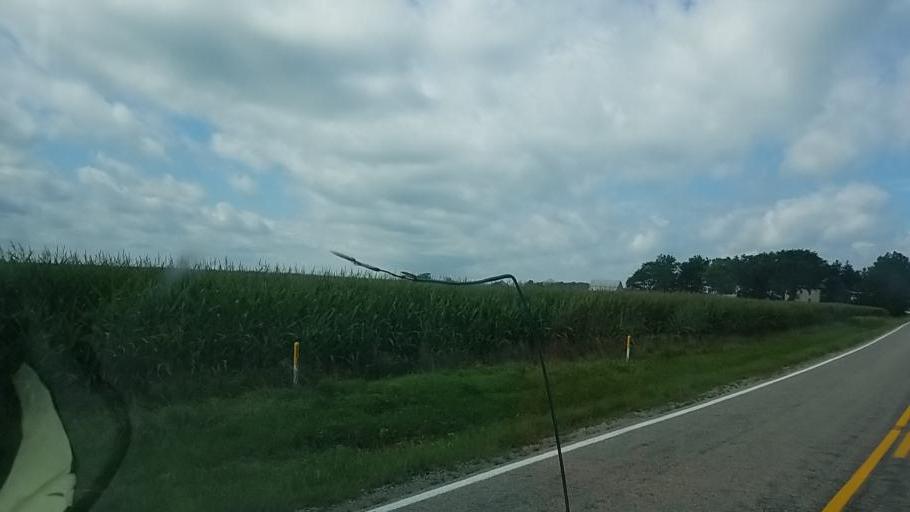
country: US
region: Ohio
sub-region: Madison County
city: Bethel
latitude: 39.7311
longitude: -83.3970
